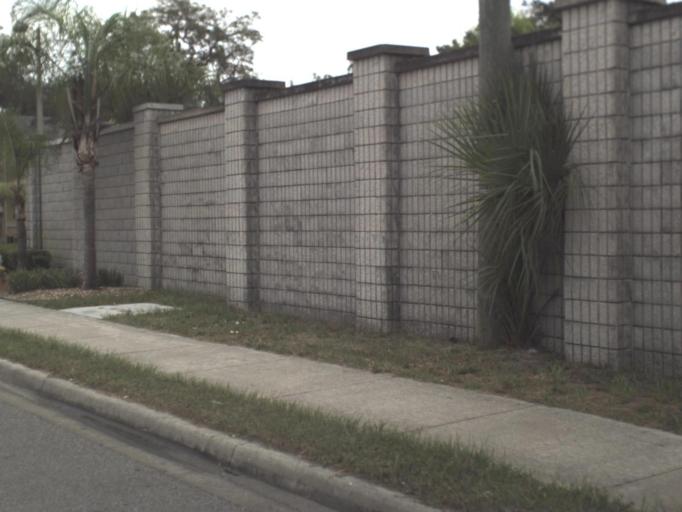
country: US
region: Florida
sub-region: Pasco County
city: Elfers
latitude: 28.2170
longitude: -82.6905
